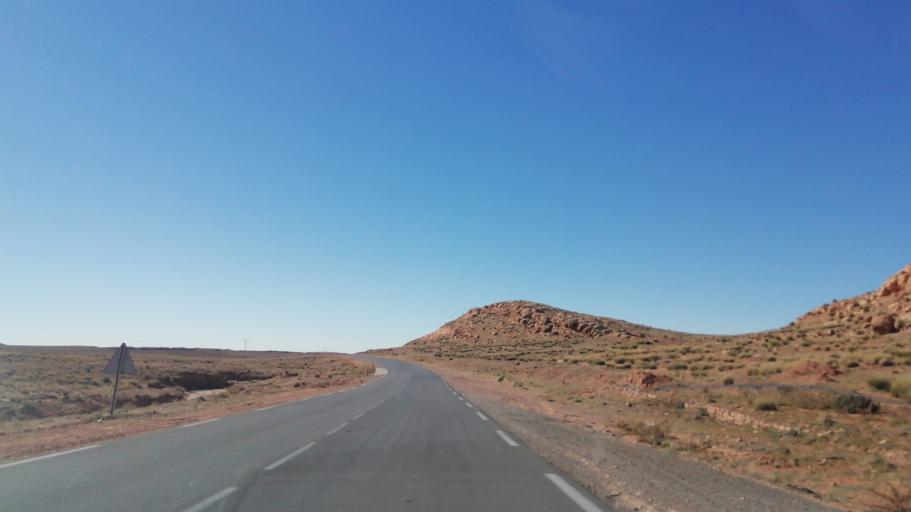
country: DZ
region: El Bayadh
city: El Bayadh
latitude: 33.6543
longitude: 1.4119
